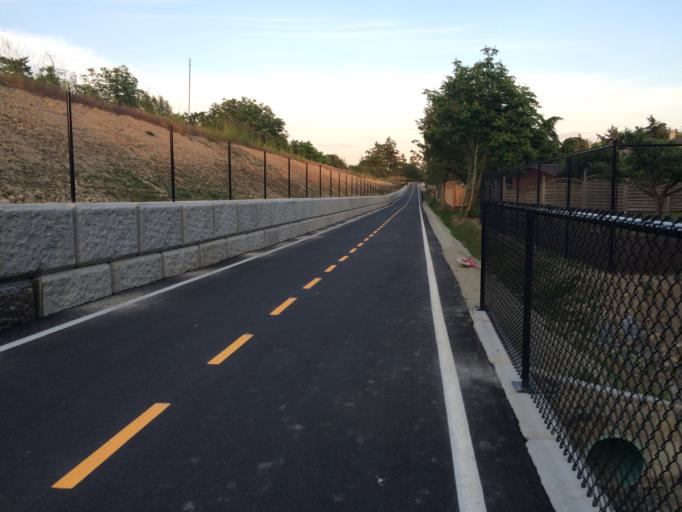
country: CA
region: British Columbia
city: Colwood
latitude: 48.4566
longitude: -123.4342
